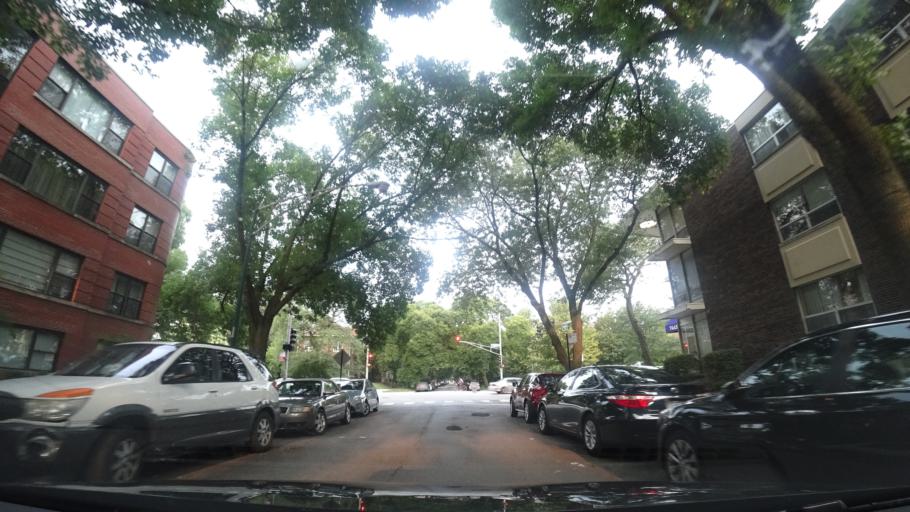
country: US
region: Illinois
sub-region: Cook County
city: Evanston
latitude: 42.0172
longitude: -87.6649
